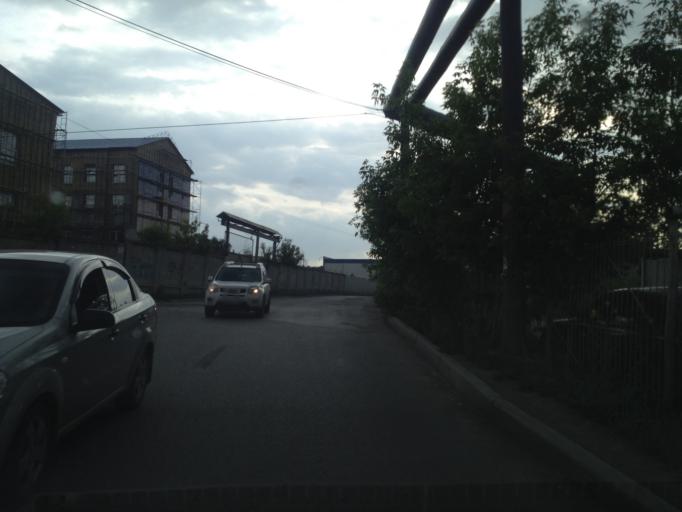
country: RU
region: Sverdlovsk
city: Yekaterinburg
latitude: 56.7884
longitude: 60.6155
